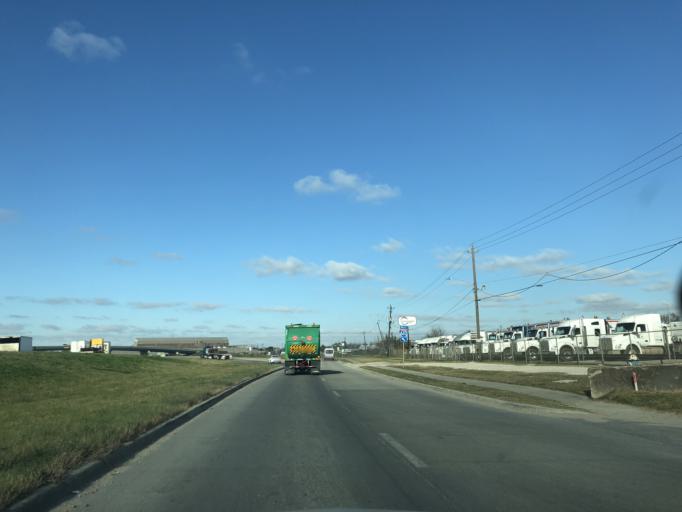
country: US
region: Texas
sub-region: Harris County
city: Houston
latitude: 29.8090
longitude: -95.3039
